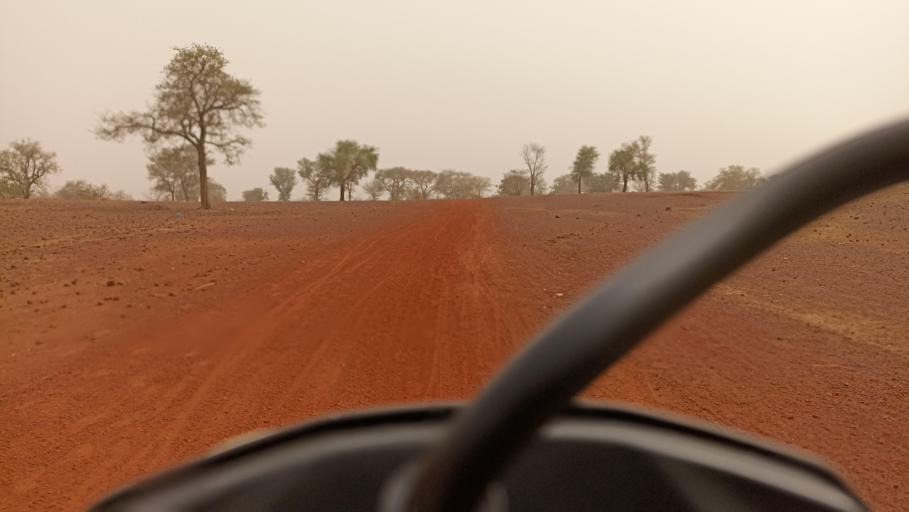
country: BF
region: Nord
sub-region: Province du Zondoma
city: Gourcy
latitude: 13.2912
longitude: -2.5230
